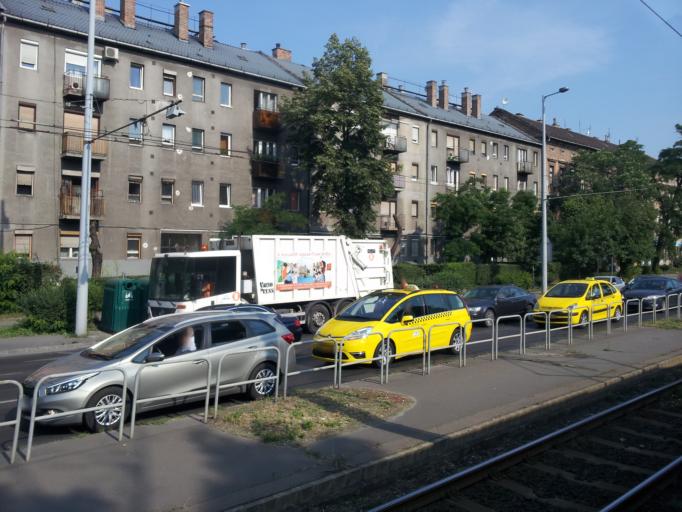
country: HU
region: Budapest
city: Budapest XIV. keruelet
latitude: 47.4924
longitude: 19.1088
